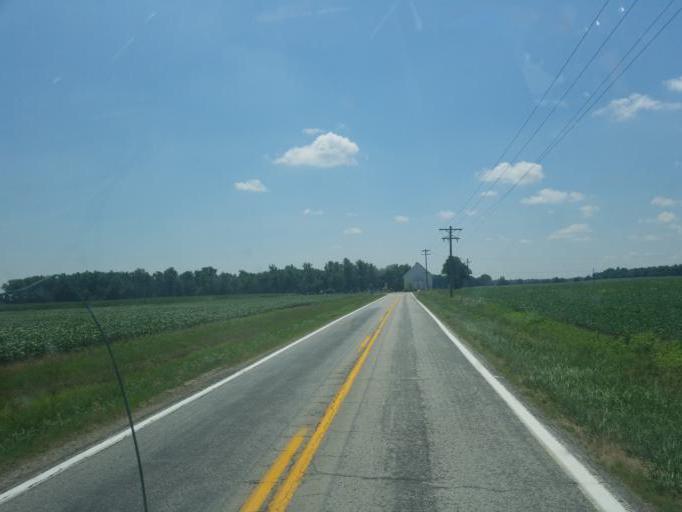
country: US
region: Ohio
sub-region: Allen County
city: Spencerville
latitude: 40.6785
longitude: -84.4255
